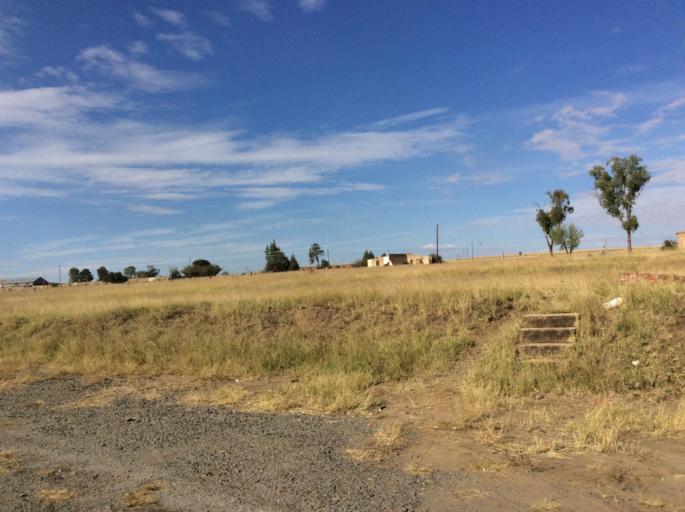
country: LS
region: Mafeteng
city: Mafeteng
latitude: -29.7323
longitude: 27.0280
